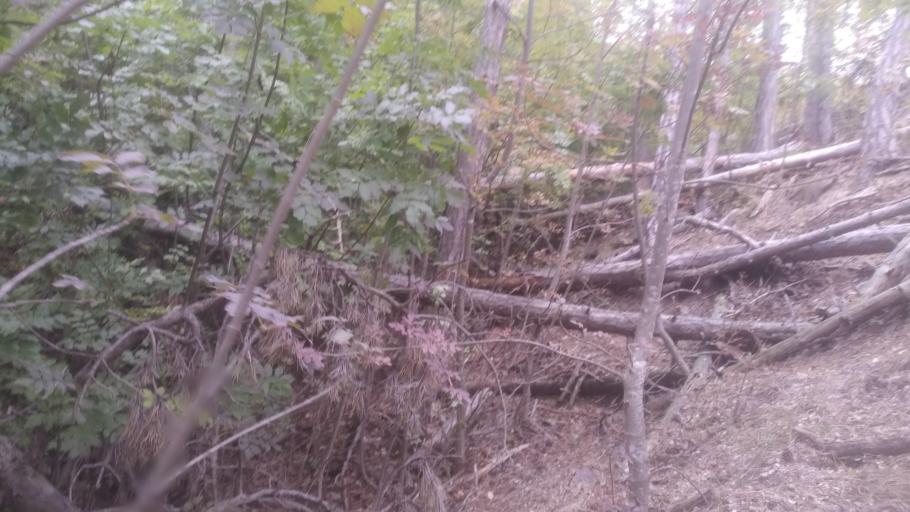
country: HU
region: Pest
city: Telki
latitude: 47.5407
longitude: 18.8699
